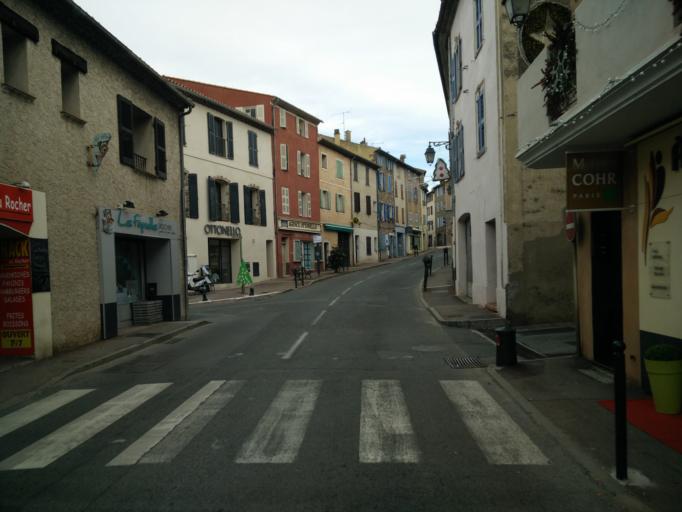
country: FR
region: Provence-Alpes-Cote d'Azur
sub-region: Departement du Var
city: Roquebrune-sur-Argens
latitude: 43.4455
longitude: 6.6373
